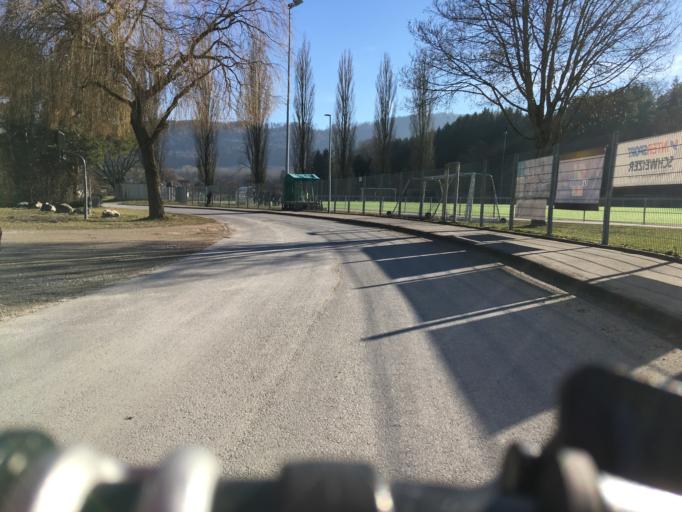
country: DE
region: Baden-Wuerttemberg
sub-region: Freiburg Region
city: Rielasingen-Worblingen
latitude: 47.7238
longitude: 8.8573
